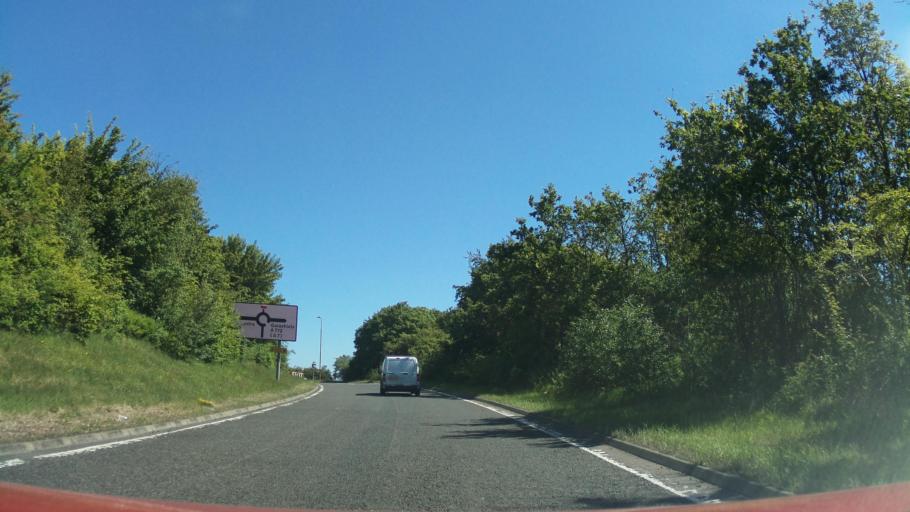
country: GB
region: Scotland
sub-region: Midlothian
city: Bonnyrigg
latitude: 55.8989
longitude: -3.1143
